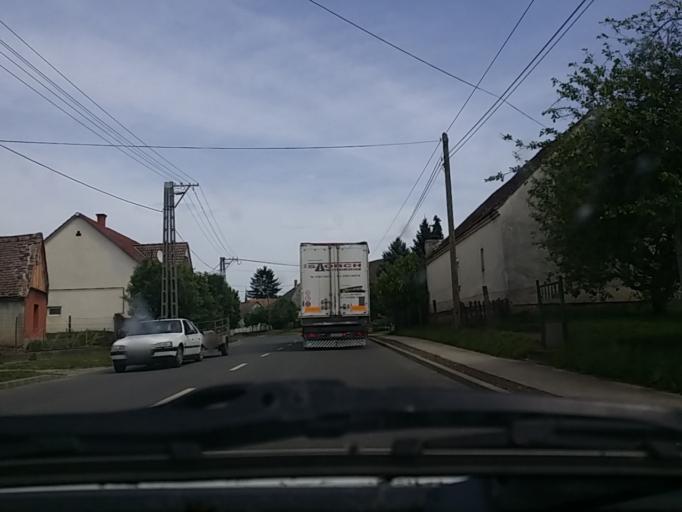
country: HU
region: Baranya
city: Sellye
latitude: 45.8817
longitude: 17.9034
